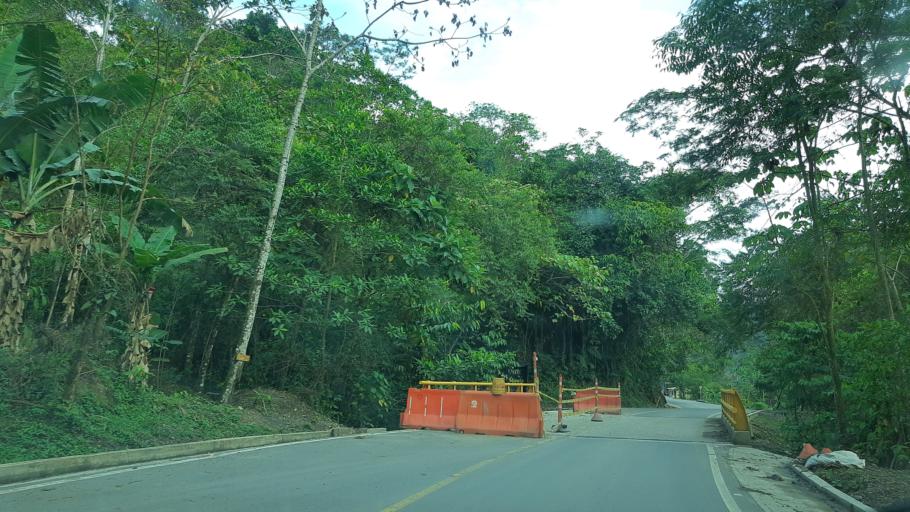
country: CO
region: Boyaca
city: Santa Maria
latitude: 4.8428
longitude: -73.2167
